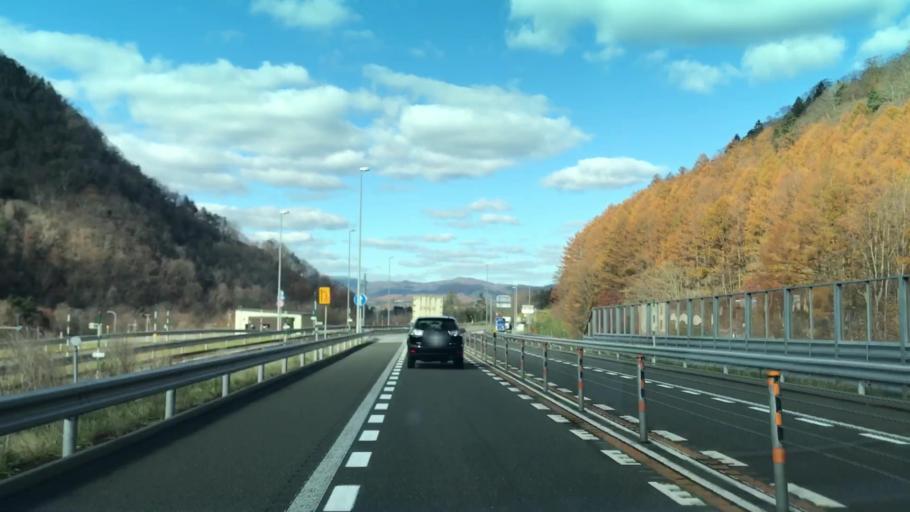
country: JP
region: Hokkaido
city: Iwamizawa
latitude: 42.9238
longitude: 142.0364
